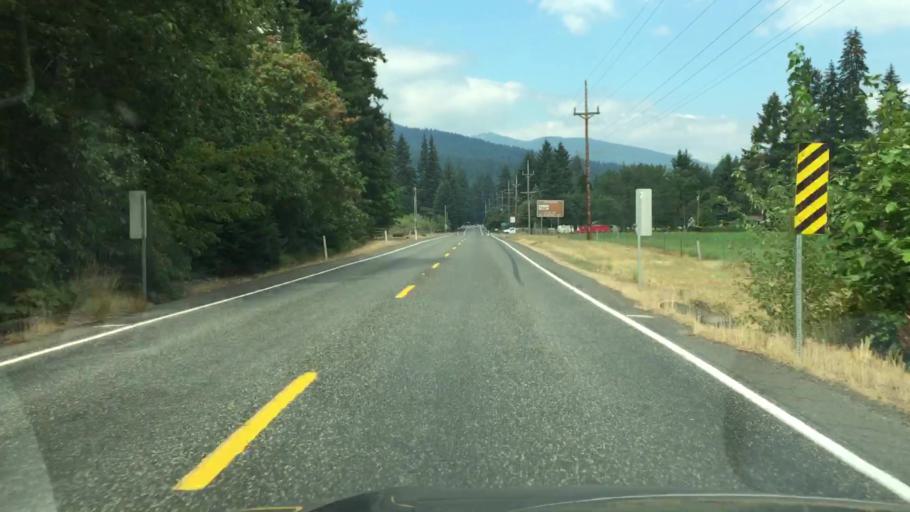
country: US
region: Washington
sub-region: Klickitat County
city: White Salmon
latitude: 45.8451
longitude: -121.5057
